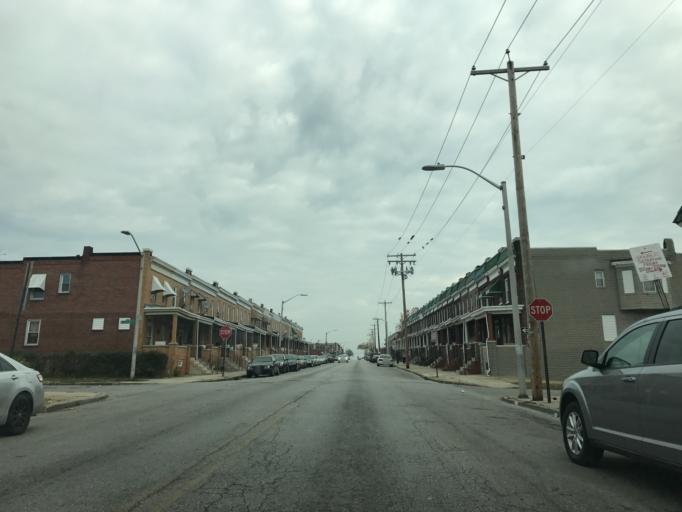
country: US
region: Maryland
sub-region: City of Baltimore
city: Baltimore
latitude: 39.3049
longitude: -76.5802
